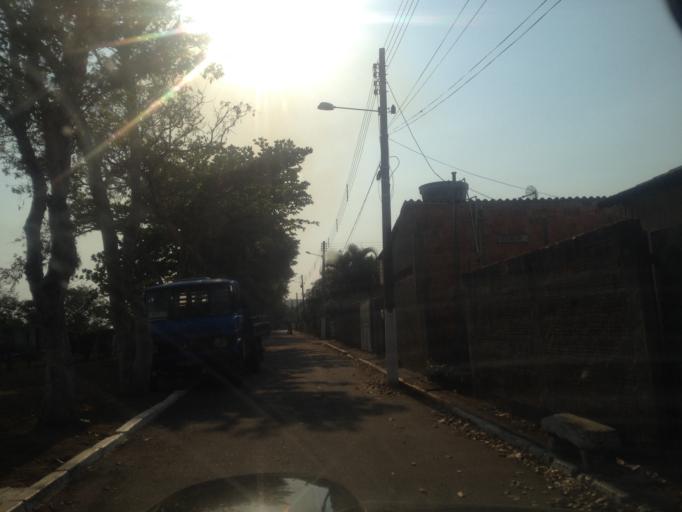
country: BR
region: Rio de Janeiro
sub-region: Porto Real
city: Porto Real
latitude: -22.4609
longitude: -44.3462
